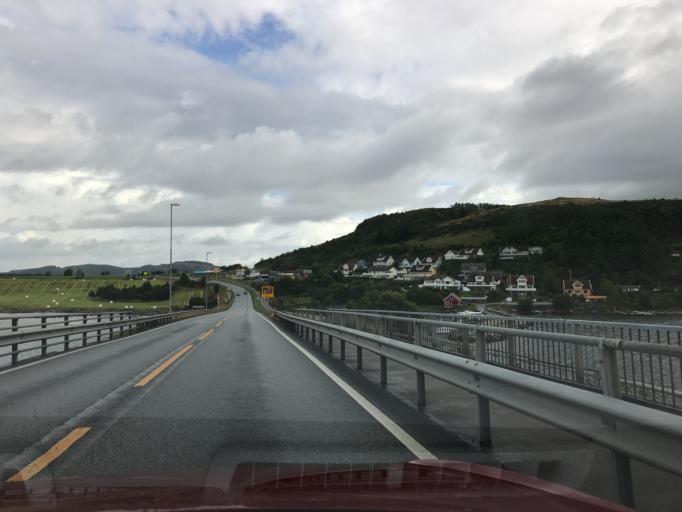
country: NO
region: Rogaland
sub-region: Rennesoy
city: Vikevag
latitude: 59.0601
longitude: 5.6773
